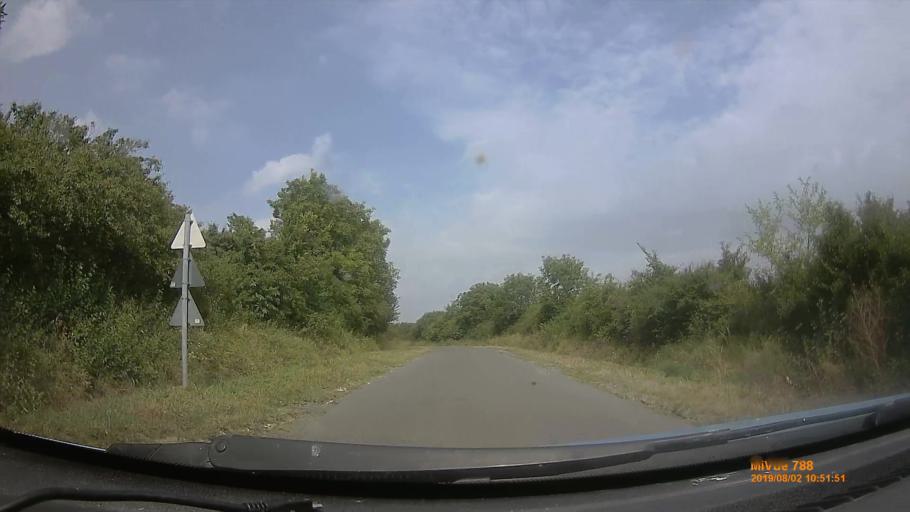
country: HU
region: Baranya
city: Buekkoesd
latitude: 46.0877
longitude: 17.9646
